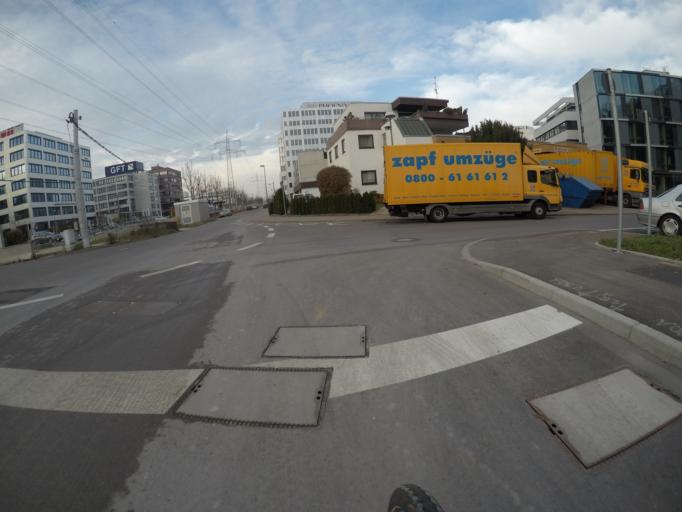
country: DE
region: Baden-Wuerttemberg
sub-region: Regierungsbezirk Stuttgart
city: Leinfelden-Echterdingen
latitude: 48.7071
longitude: 9.1711
